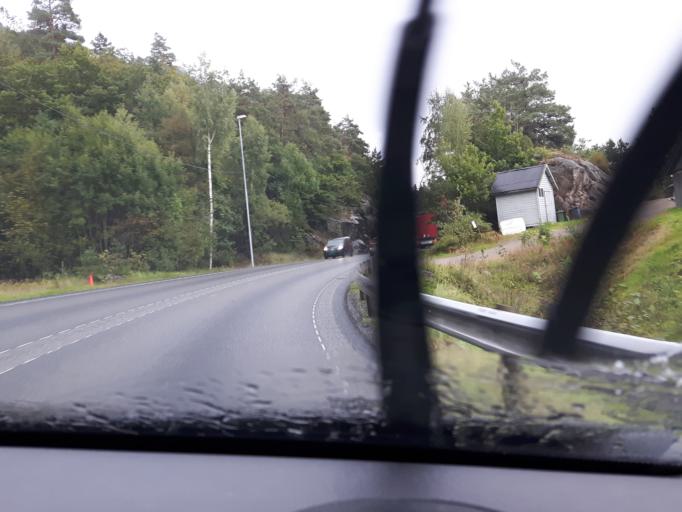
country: NO
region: Vest-Agder
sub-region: Sogne
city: Sogne
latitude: 58.0957
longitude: 7.6889
